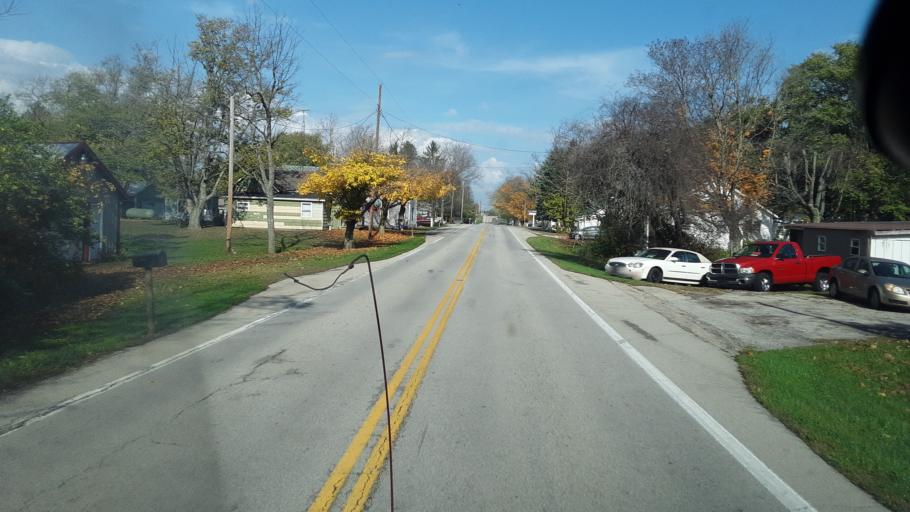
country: US
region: Ohio
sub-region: Clinton County
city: Sabina
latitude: 39.5360
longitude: -83.7053
